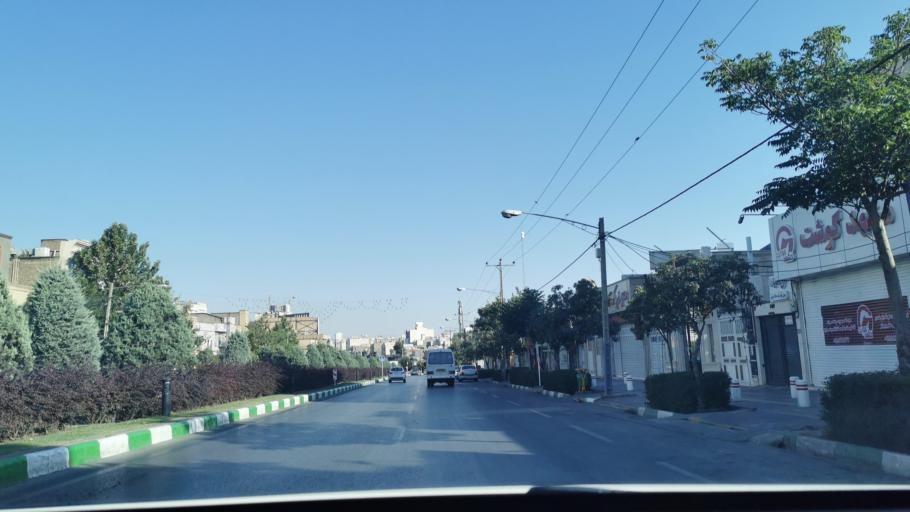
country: IR
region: Razavi Khorasan
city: Mashhad
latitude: 36.3091
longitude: 59.5065
